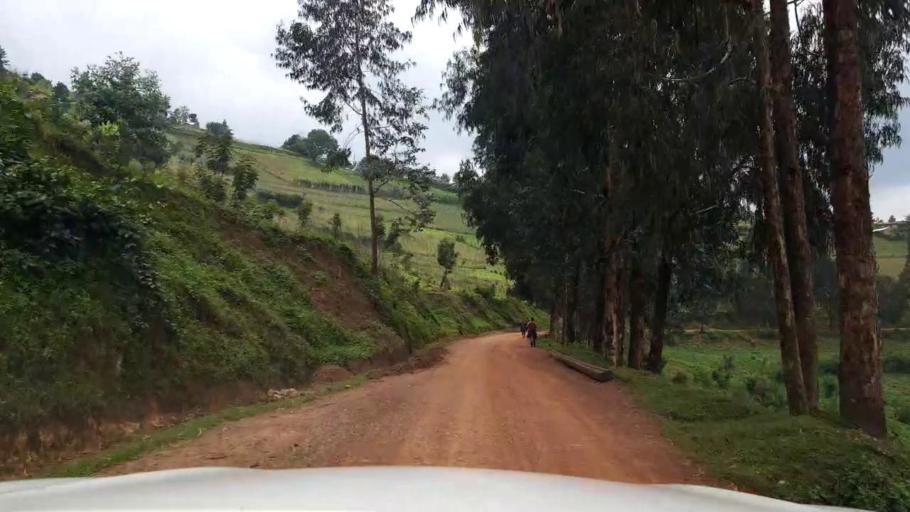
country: UG
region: Western Region
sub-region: Kabale District
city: Kabale
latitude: -1.4284
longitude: 29.8676
